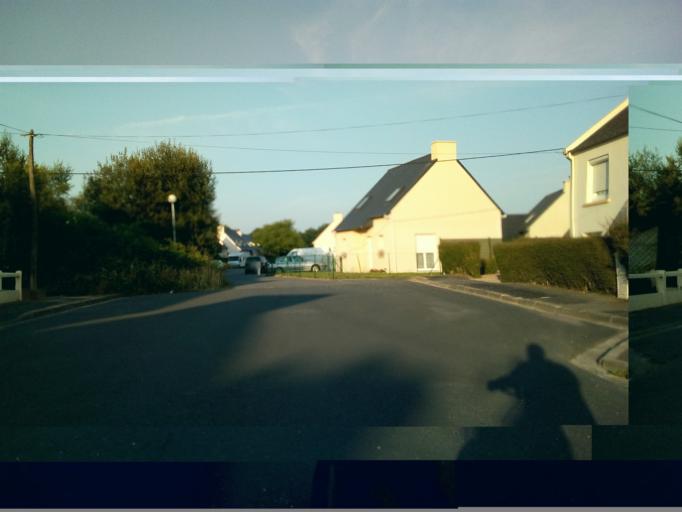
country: FR
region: Brittany
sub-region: Departement du Finistere
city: Landivisiau
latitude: 48.5027
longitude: -4.0752
